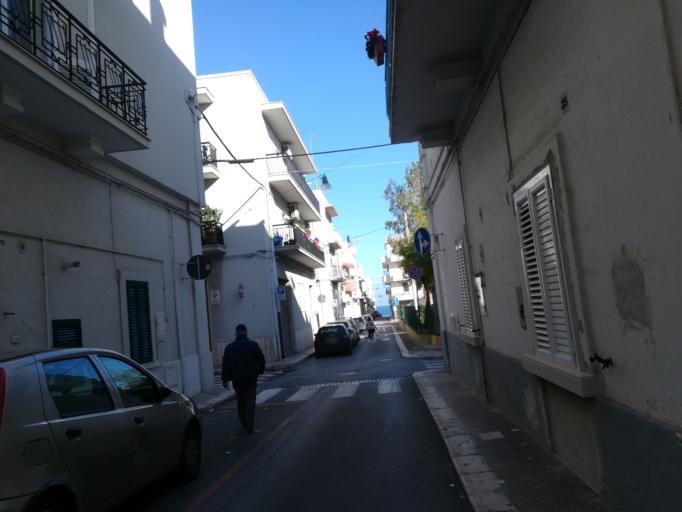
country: IT
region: Apulia
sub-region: Provincia di Bari
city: Polignano a Mare
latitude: 40.9941
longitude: 17.2244
